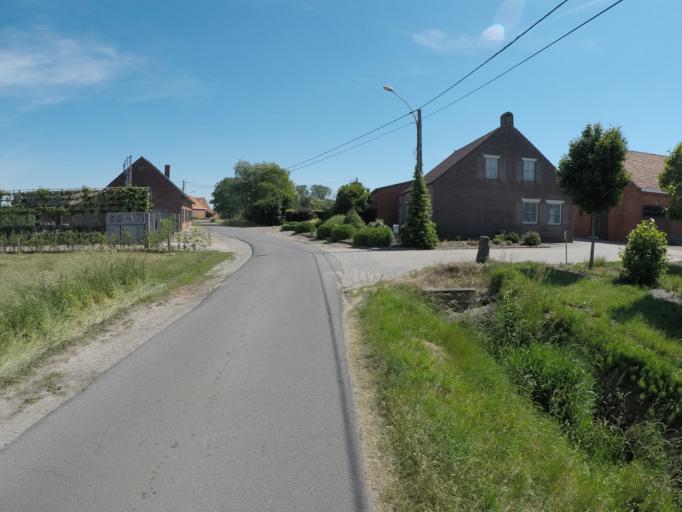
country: NL
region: North Brabant
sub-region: Gemeente Zundert
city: Zundert
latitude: 51.4132
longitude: 4.6565
